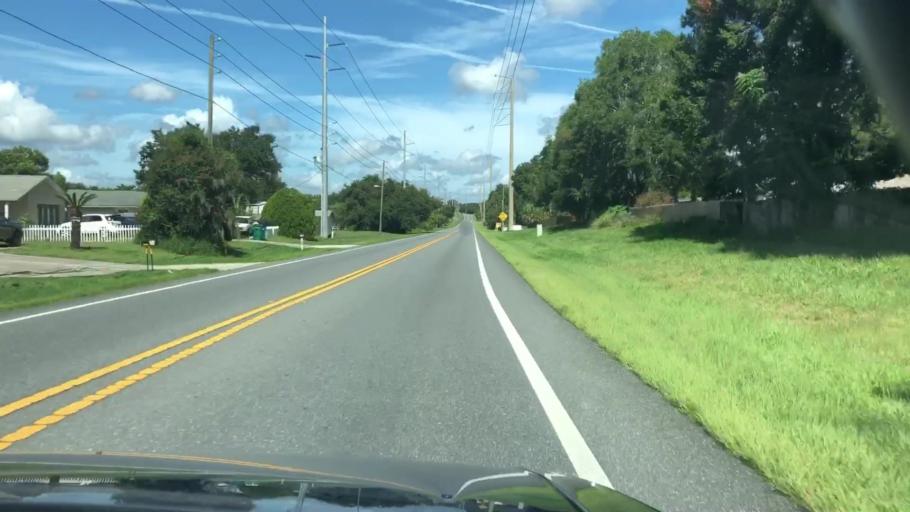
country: US
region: Florida
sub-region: Lake County
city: Eustis
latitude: 28.8779
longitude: -81.7123
